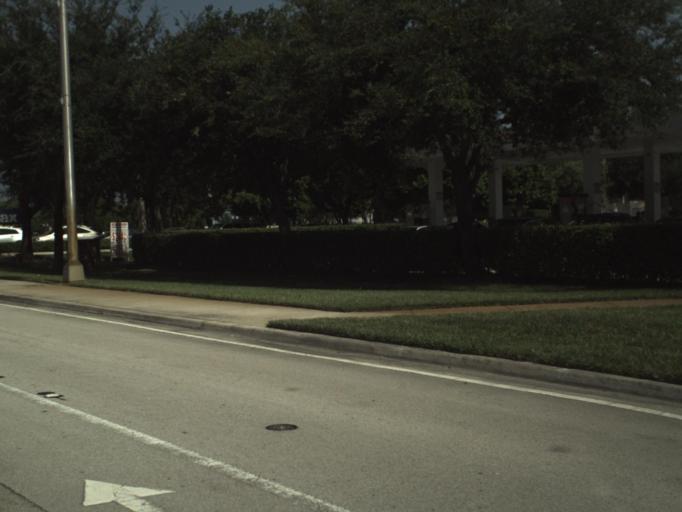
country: US
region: Florida
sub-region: Broward County
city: Tedder
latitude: 26.2744
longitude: -80.1486
